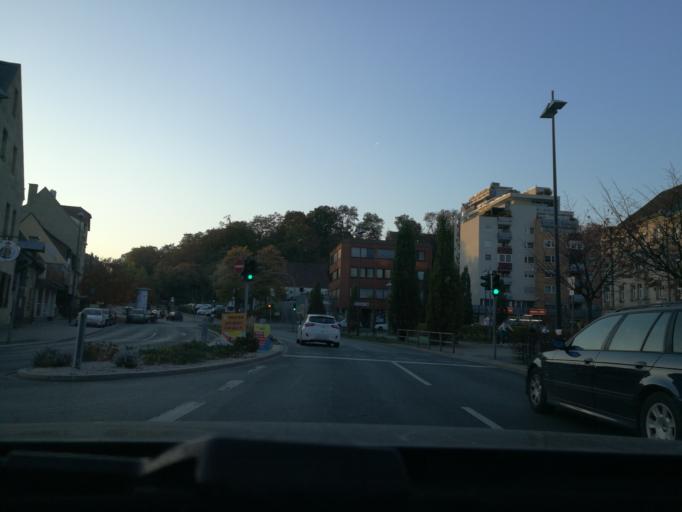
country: DE
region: Bavaria
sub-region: Regierungsbezirk Mittelfranken
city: Furth
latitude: 49.4805
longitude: 10.9775
